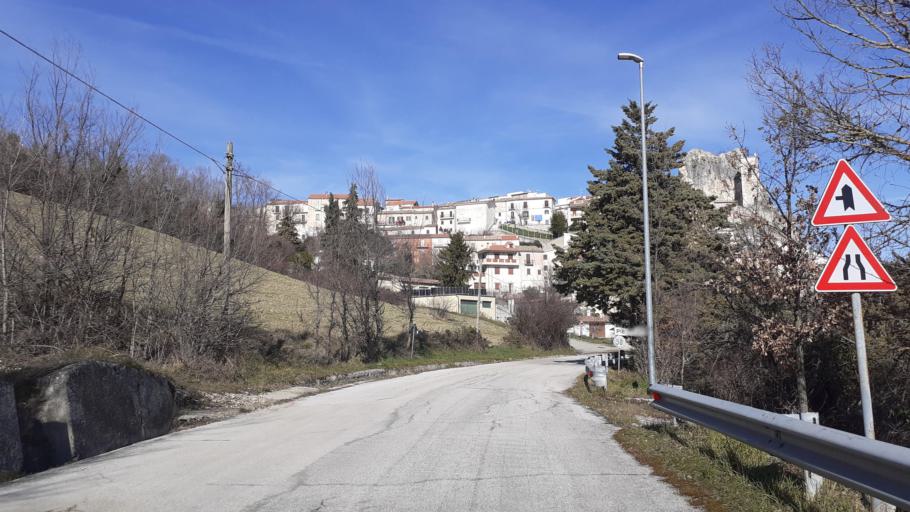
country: IT
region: Molise
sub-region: Provincia di Campobasso
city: Pietracupa
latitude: 41.6804
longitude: 14.5194
